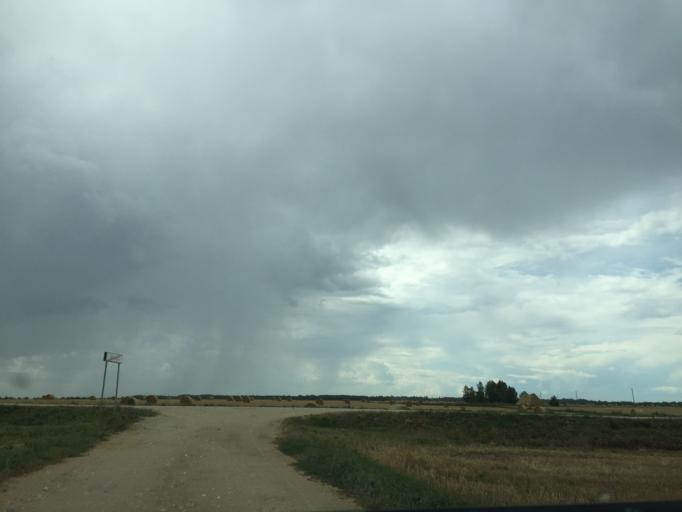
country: LT
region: Siauliu apskritis
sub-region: Joniskis
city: Joniskis
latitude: 56.2840
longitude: 23.7231
